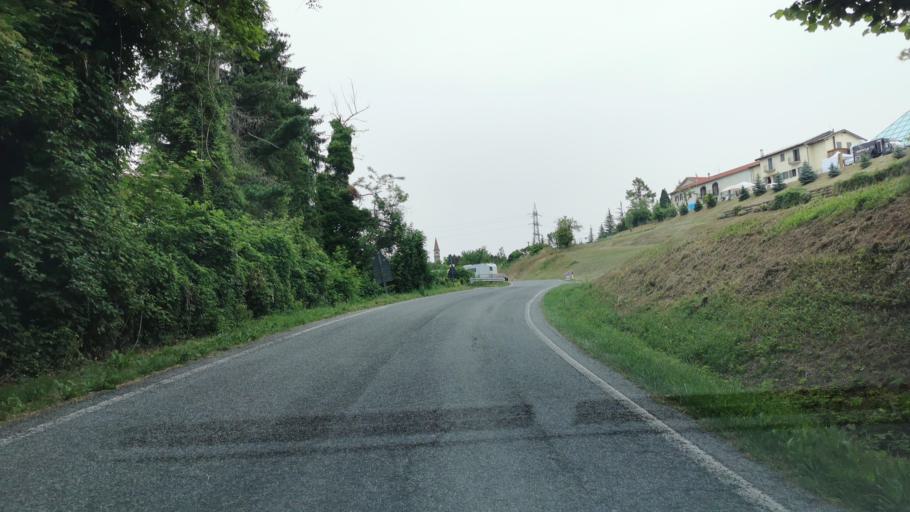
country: IT
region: Piedmont
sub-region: Provincia di Cuneo
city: Sale San Giovanni
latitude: 44.4007
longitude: 8.0772
